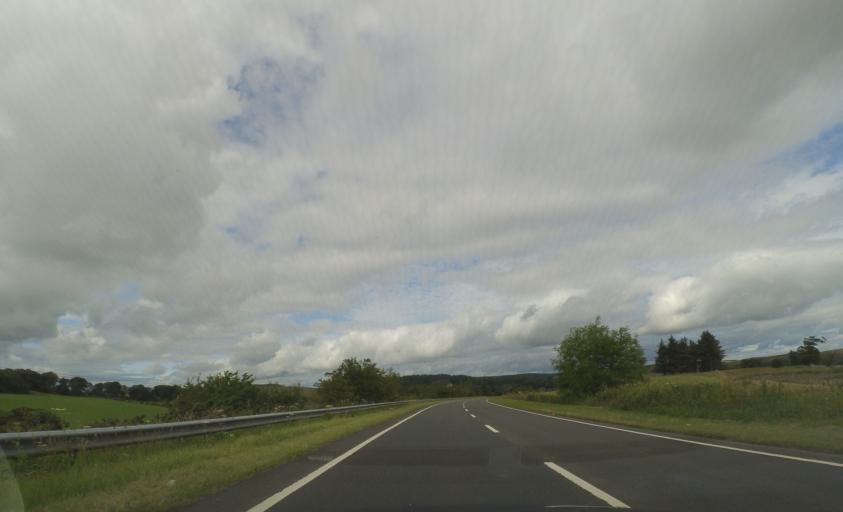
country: GB
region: Scotland
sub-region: The Scottish Borders
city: Selkirk
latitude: 55.4826
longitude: -2.8291
